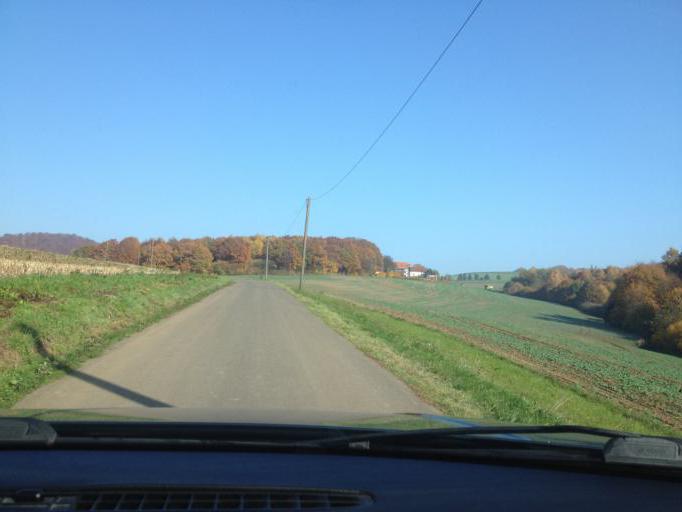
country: DE
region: Saarland
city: Sankt Wendel
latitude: 49.4963
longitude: 7.1947
